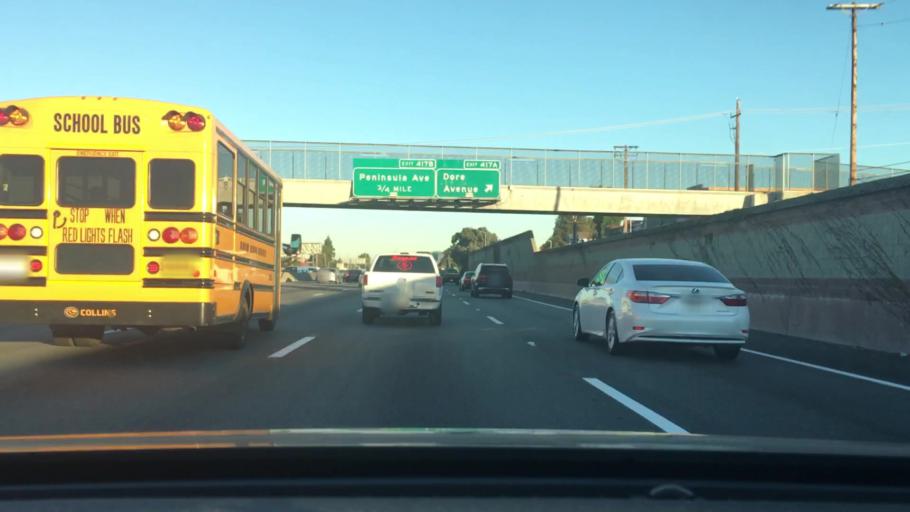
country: US
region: California
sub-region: San Mateo County
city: San Mateo
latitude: 37.5759
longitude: -122.3192
